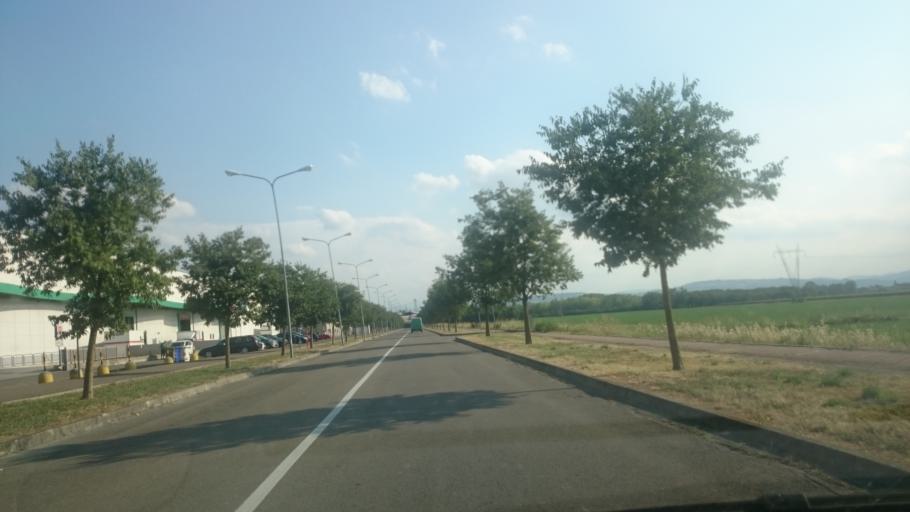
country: IT
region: Emilia-Romagna
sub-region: Provincia di Reggio Emilia
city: Rubiera
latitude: 44.6459
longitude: 10.7727
